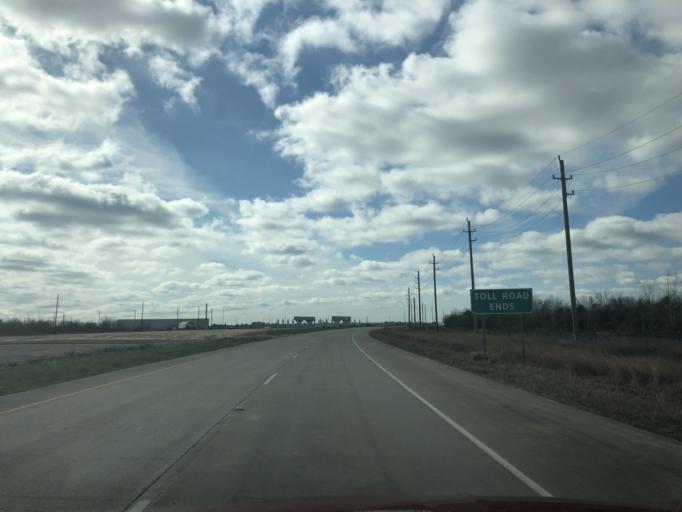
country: US
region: Texas
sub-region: Chambers County
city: Beach City
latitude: 29.7351
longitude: -94.8749
